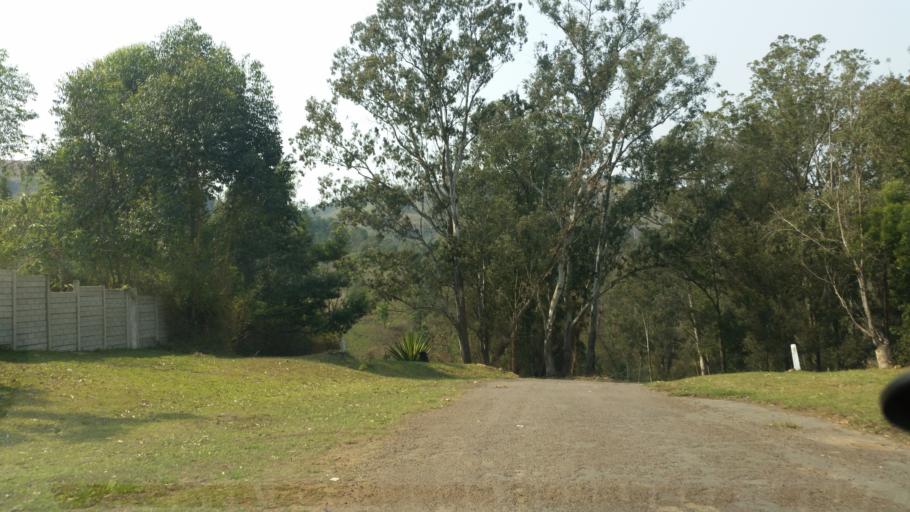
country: ZA
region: KwaZulu-Natal
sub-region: eThekwini Metropolitan Municipality
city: Mpumalanga
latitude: -29.7404
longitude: 30.6636
